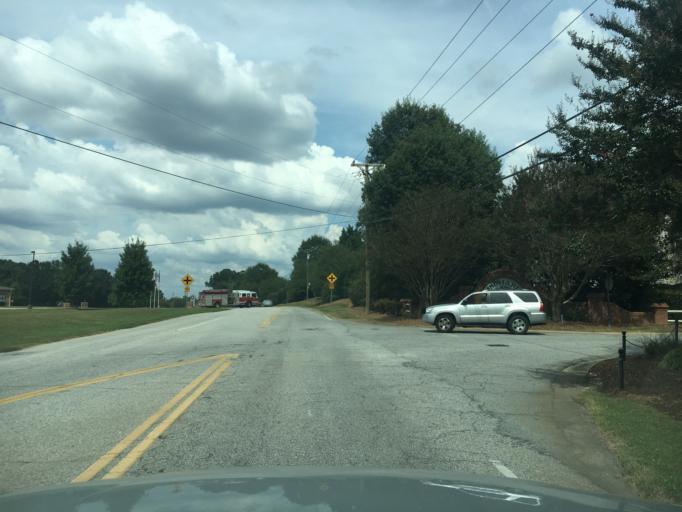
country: US
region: South Carolina
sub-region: Greenville County
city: Five Forks
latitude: 34.8268
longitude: -82.2282
